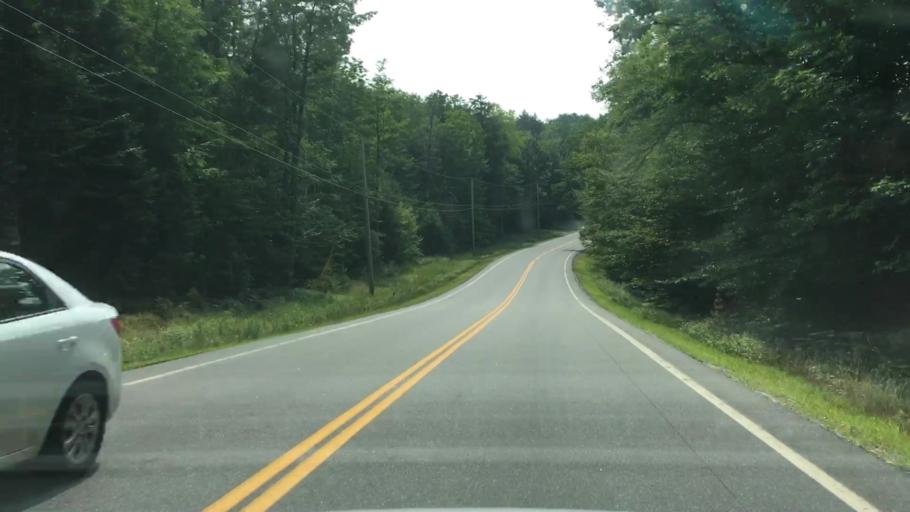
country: US
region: Maine
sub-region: Oxford County
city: Buckfield
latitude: 44.2680
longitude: -70.4162
